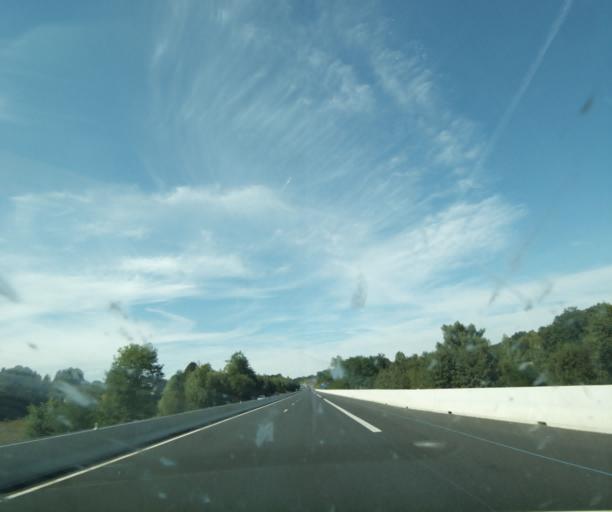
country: FR
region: Limousin
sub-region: Departement de la Correze
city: Saint-Mexant
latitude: 45.2952
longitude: 1.5949
